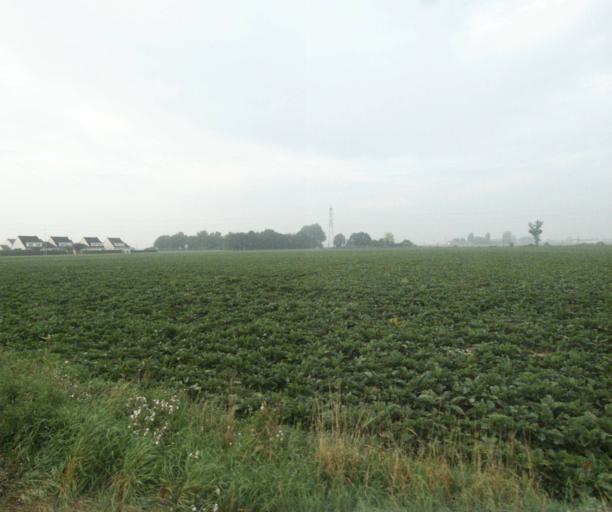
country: FR
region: Nord-Pas-de-Calais
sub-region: Departement du Nord
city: Seclin
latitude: 50.5438
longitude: 3.0118
